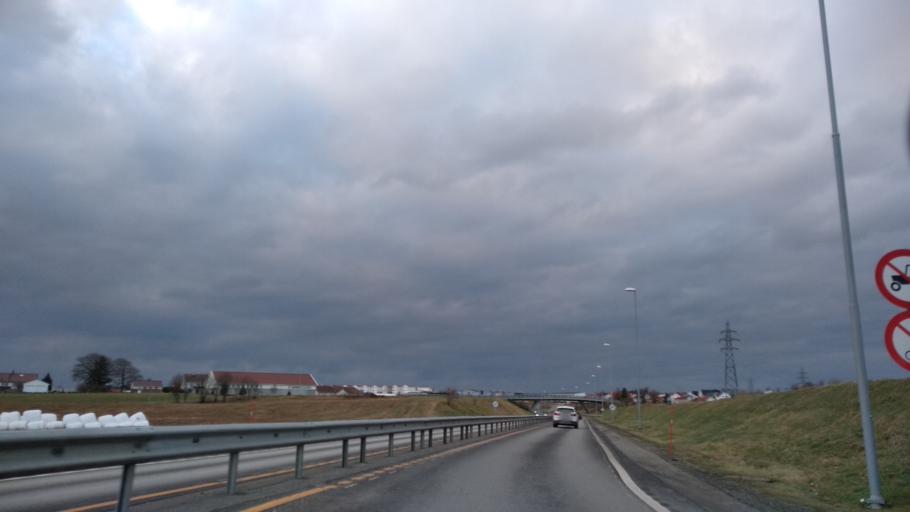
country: NO
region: Rogaland
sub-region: Klepp
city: Kleppe
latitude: 58.7843
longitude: 5.6378
